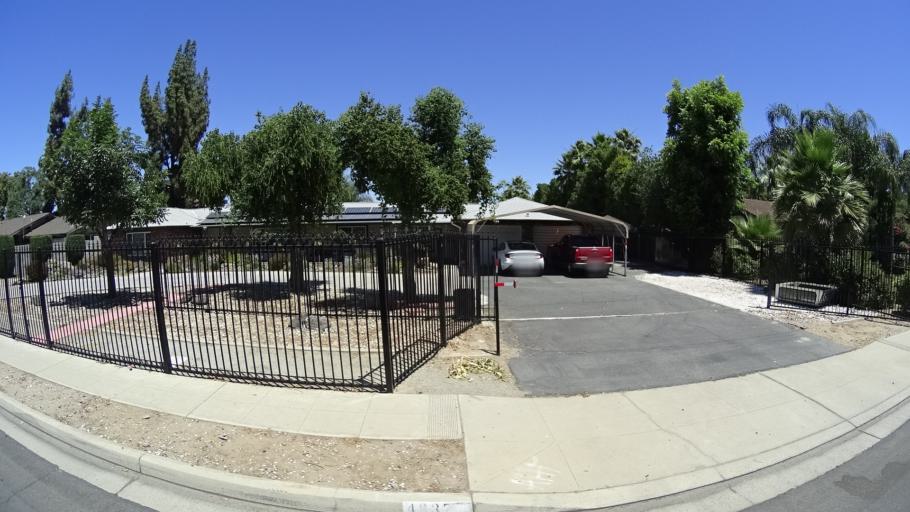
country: US
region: California
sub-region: Fresno County
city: Tarpey Village
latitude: 36.7723
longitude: -119.7345
